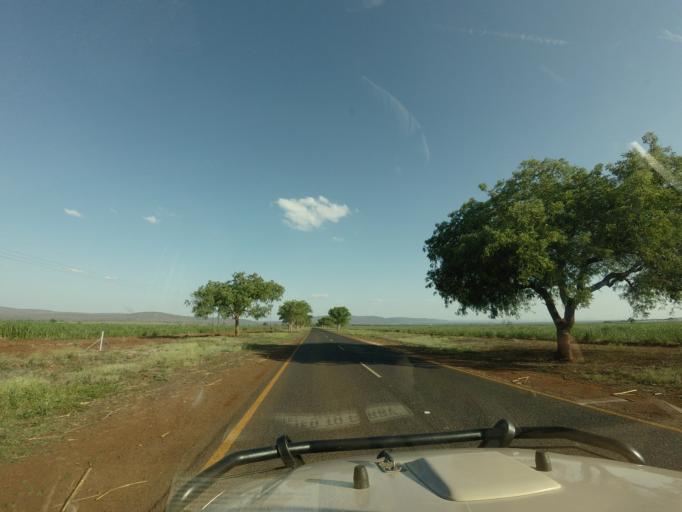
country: ZA
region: Mpumalanga
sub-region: Ehlanzeni District
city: Komatipoort
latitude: -25.4013
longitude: 31.9226
